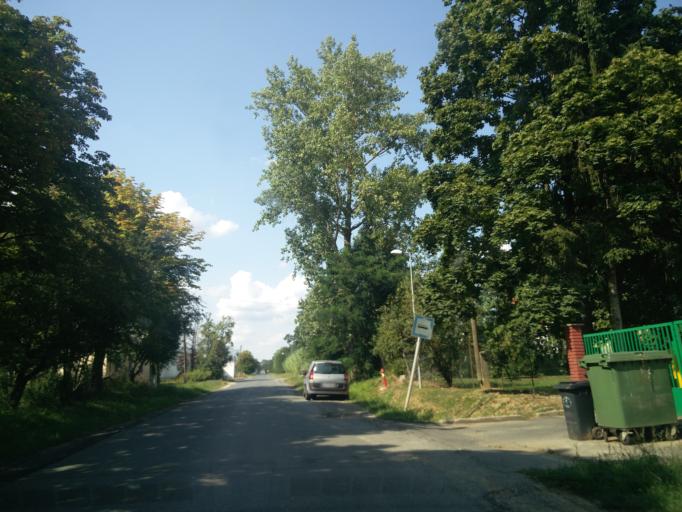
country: HU
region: Zala
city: Zalaegerszeg
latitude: 46.8825
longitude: 16.7936
